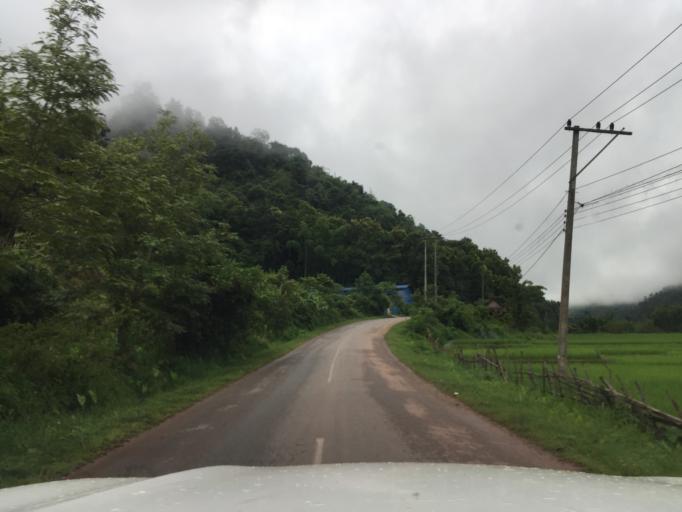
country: LA
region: Oudomxai
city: Muang La
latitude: 20.8378
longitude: 102.1029
